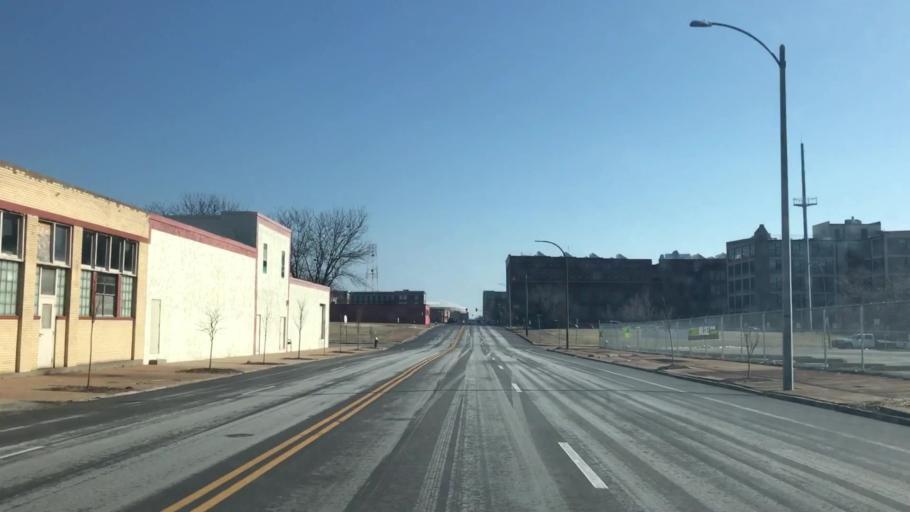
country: US
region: Missouri
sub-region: City of Saint Louis
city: St. Louis
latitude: 38.6364
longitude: -90.2111
